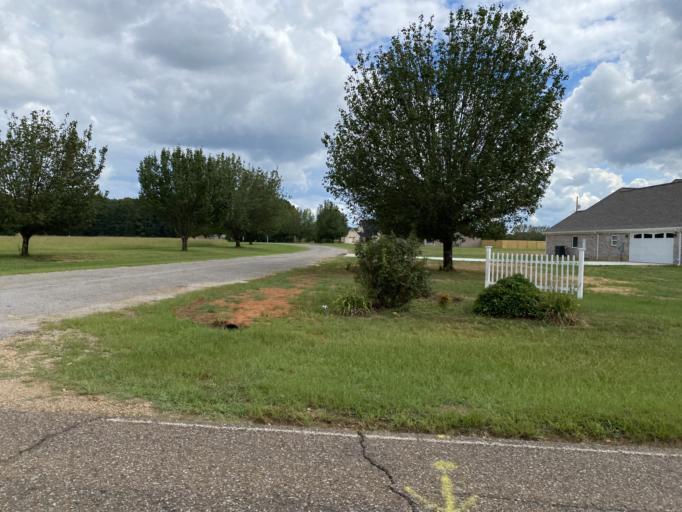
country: US
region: Mississippi
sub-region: Monroe County
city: Amory
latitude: 33.9745
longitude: -88.4448
